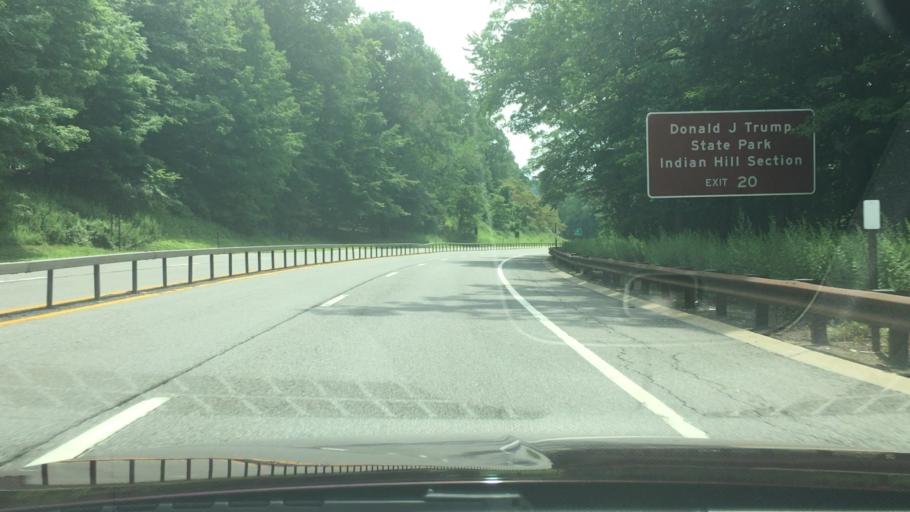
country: US
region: New York
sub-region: Westchester County
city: Shrub Oak
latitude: 41.3417
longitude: -73.8131
